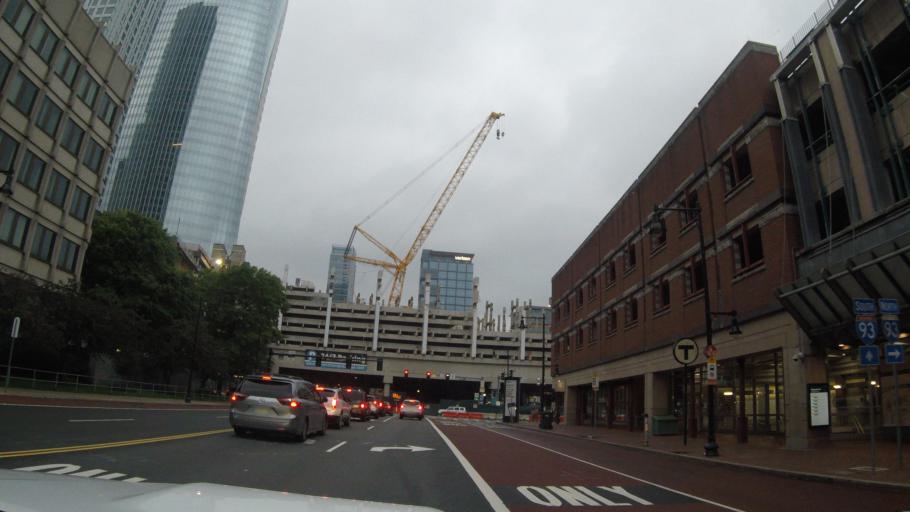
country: US
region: Massachusetts
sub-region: Suffolk County
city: Boston
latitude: 42.3620
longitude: -71.0580
